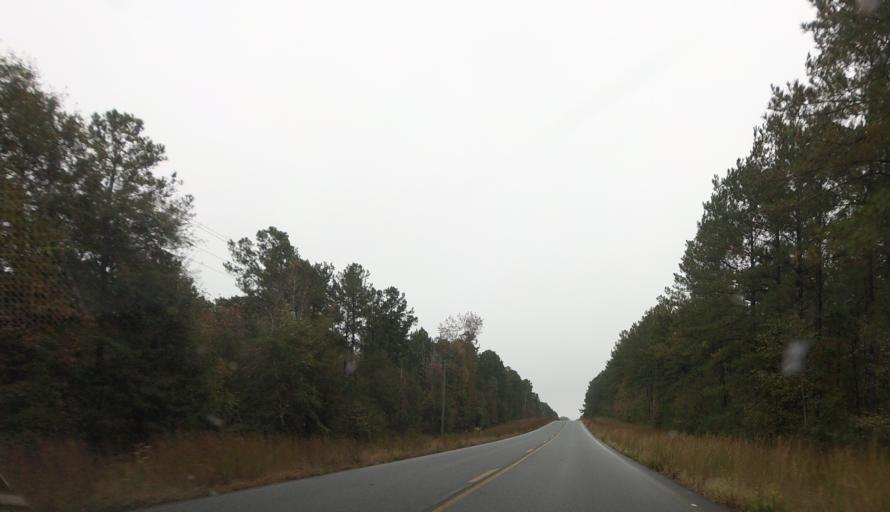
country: US
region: Georgia
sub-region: Marion County
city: Buena Vista
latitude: 32.3958
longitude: -84.4225
